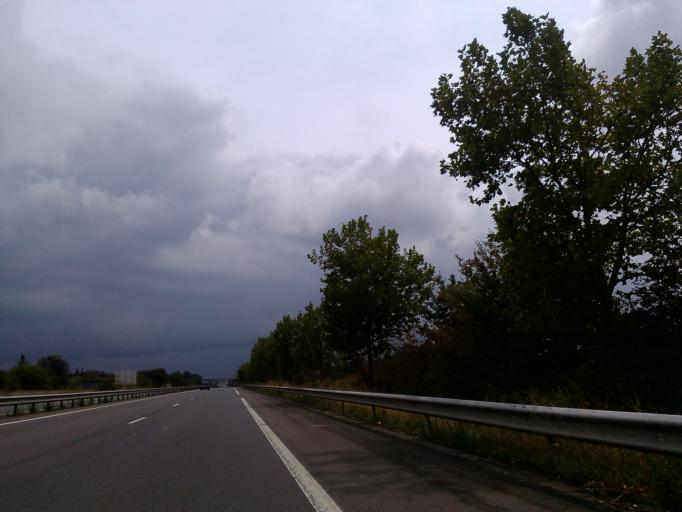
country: FR
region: Poitou-Charentes
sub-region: Departement de la Charente
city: Saint-Brice
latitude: 45.6787
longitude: -0.2826
